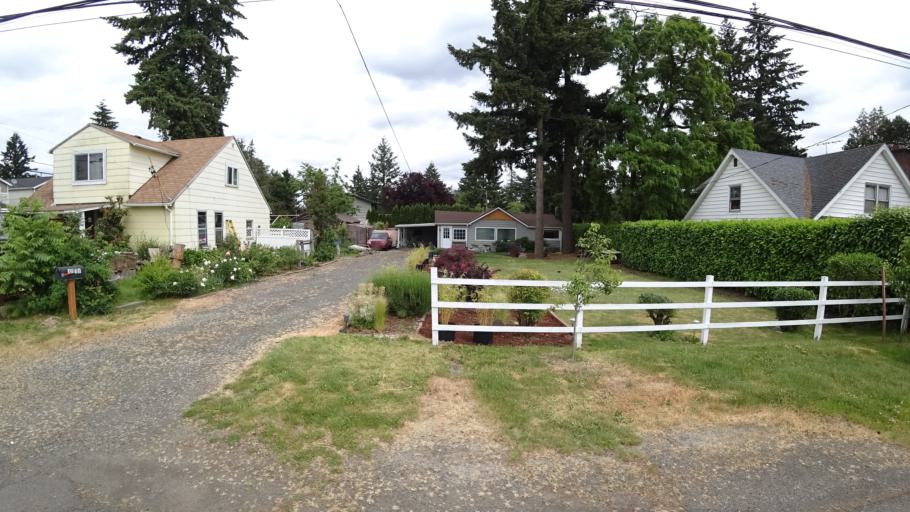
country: US
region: Oregon
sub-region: Multnomah County
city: Lents
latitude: 45.4648
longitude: -122.5874
